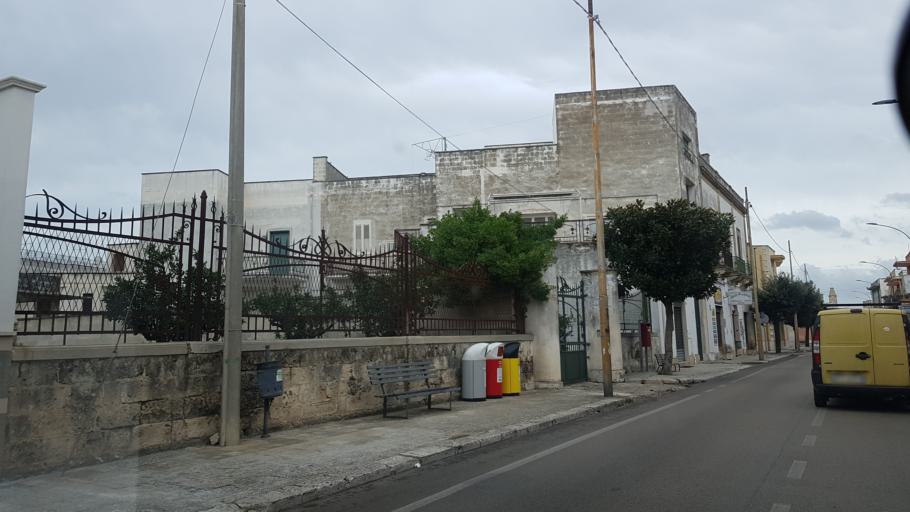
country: IT
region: Apulia
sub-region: Provincia di Lecce
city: Guagnano
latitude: 40.4008
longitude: 17.9471
